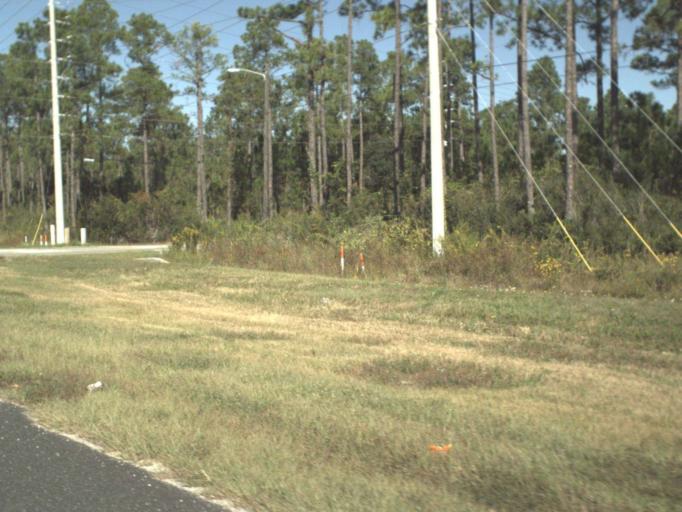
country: US
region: Florida
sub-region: Walton County
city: Seaside
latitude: 30.3674
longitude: -86.1869
